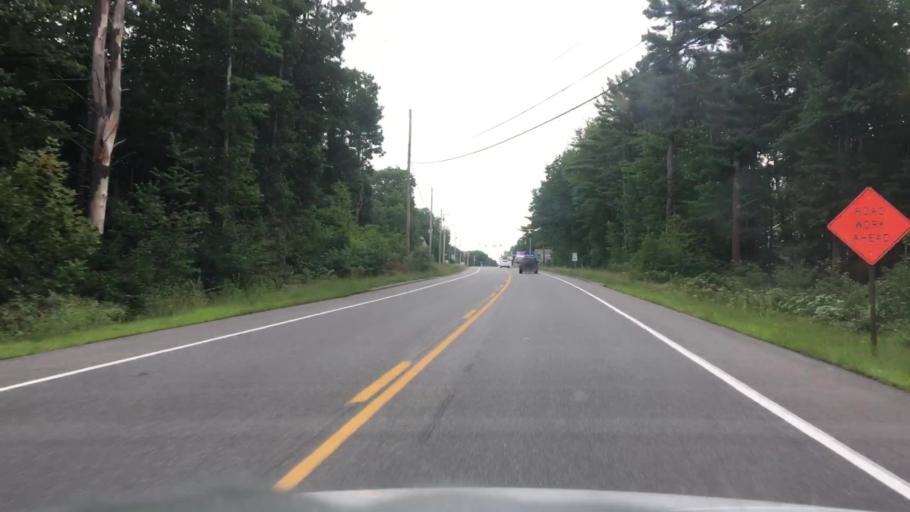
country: US
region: Maine
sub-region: York County
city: Wells Beach Station
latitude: 43.3337
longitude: -70.6282
